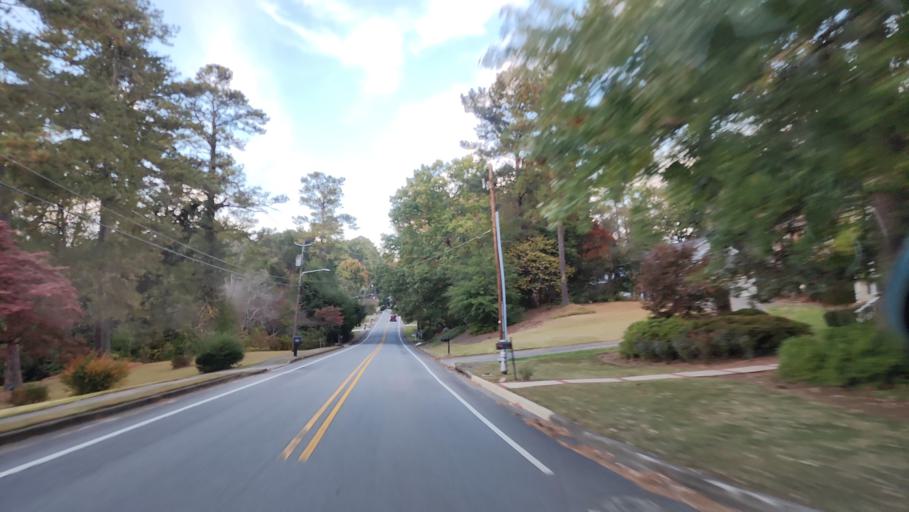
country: US
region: Georgia
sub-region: Fulton County
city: Roswell
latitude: 34.0277
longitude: -84.3705
